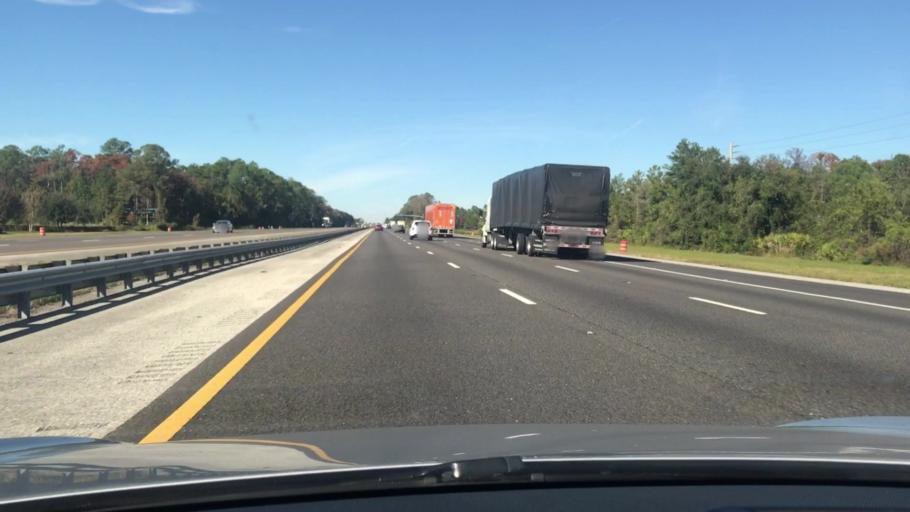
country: US
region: Florida
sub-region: Flagler County
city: Flagler Beach
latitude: 29.4822
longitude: -81.1860
